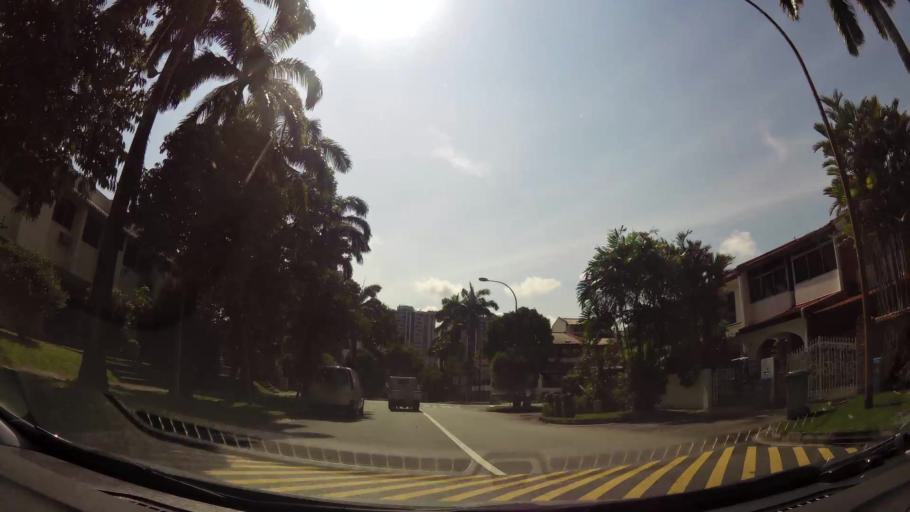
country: SG
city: Singapore
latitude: 1.3782
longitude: 103.8320
